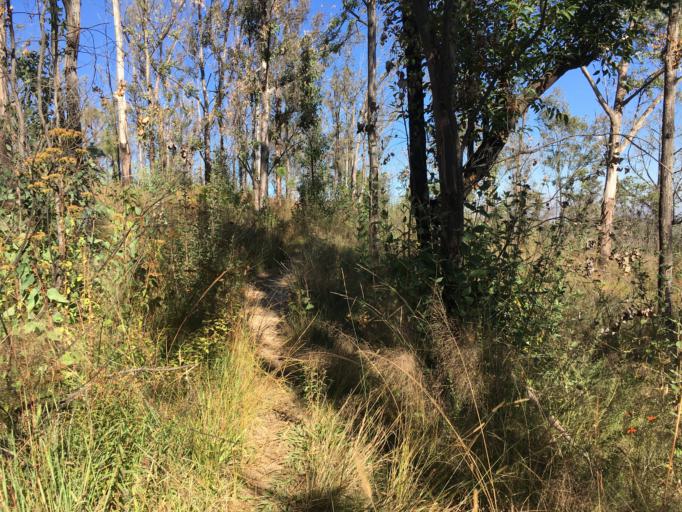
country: MX
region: Michoacan
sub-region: Morelia
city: Montana Monarca (Punta Altozano)
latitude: 19.6687
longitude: -101.1480
